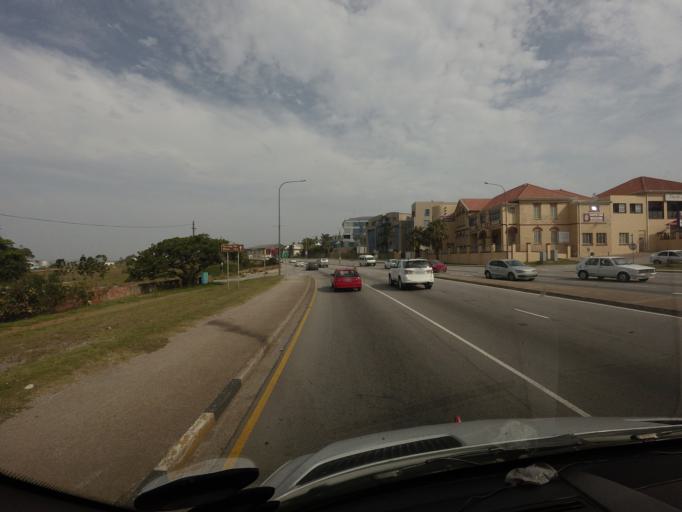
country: ZA
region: Eastern Cape
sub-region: Nelson Mandela Bay Metropolitan Municipality
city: Port Elizabeth
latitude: -33.9689
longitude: 25.6294
